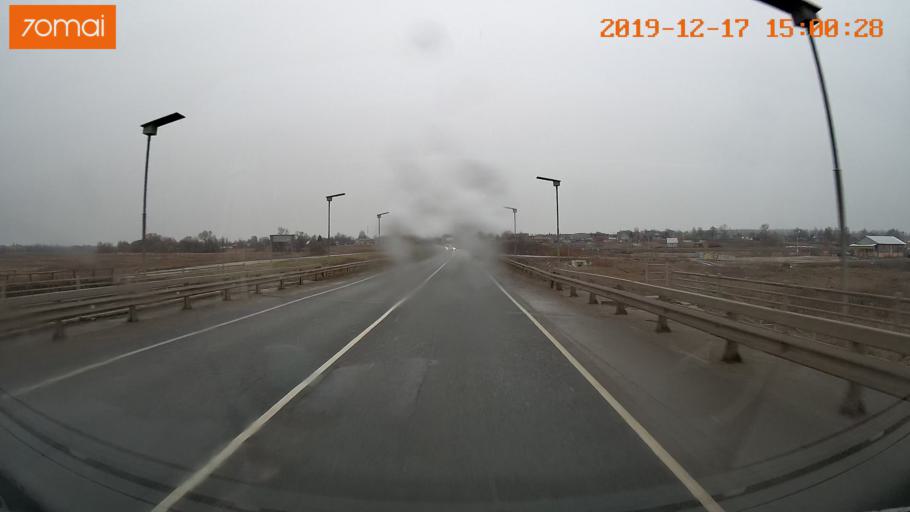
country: RU
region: Rjazan
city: Zakharovo
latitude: 54.2925
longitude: 39.1880
